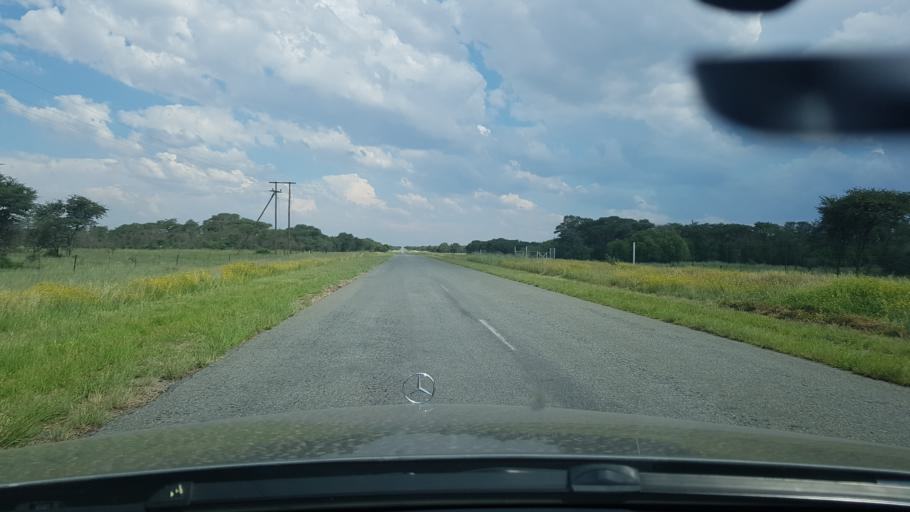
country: ZA
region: North-West
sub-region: Dr Ruth Segomotsi Mompati District Municipality
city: Bloemhof
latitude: -27.7739
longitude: 25.6053
